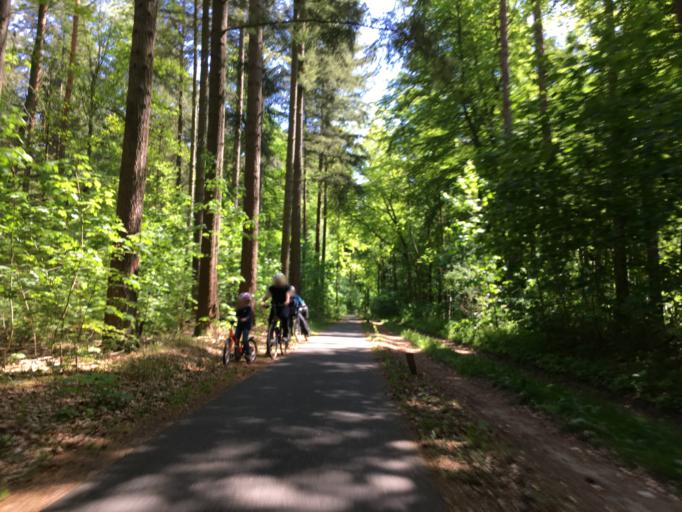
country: DE
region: Brandenburg
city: Niederfinow
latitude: 52.8509
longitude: 13.8800
